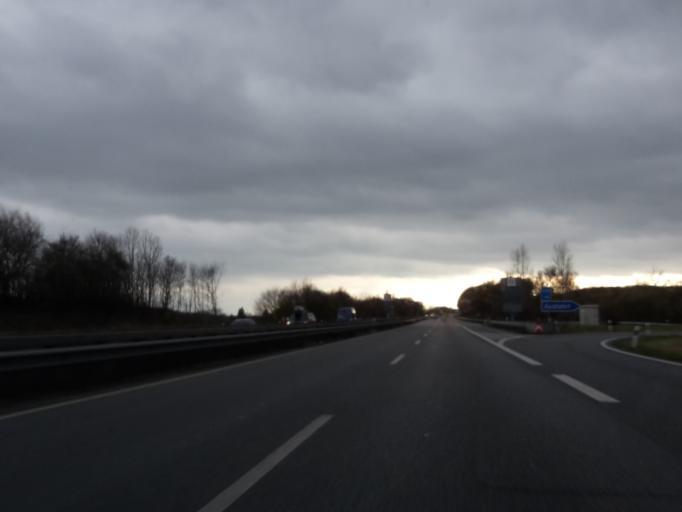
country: DE
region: Rheinland-Pfalz
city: Nieder-Olm
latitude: 49.9132
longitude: 8.1929
